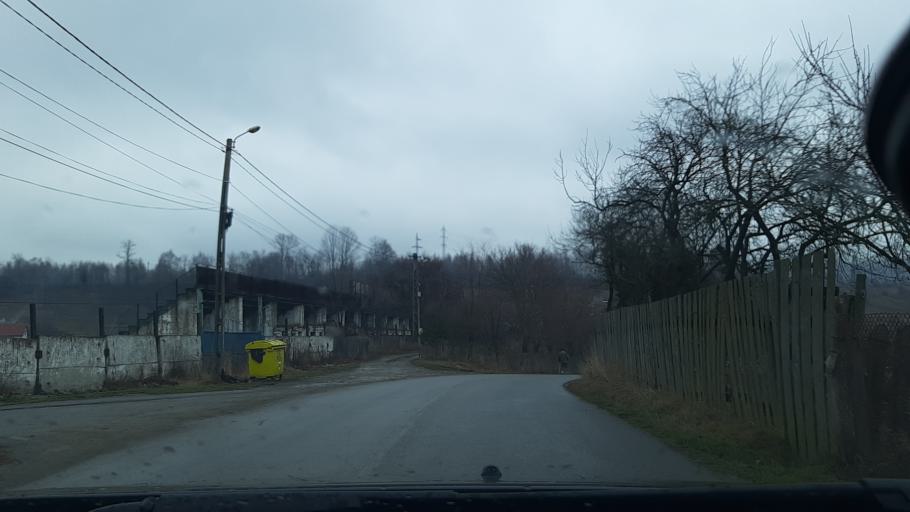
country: RO
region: Hunedoara
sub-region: Oras Petrila
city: Petrila
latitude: 45.4400
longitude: 23.4122
